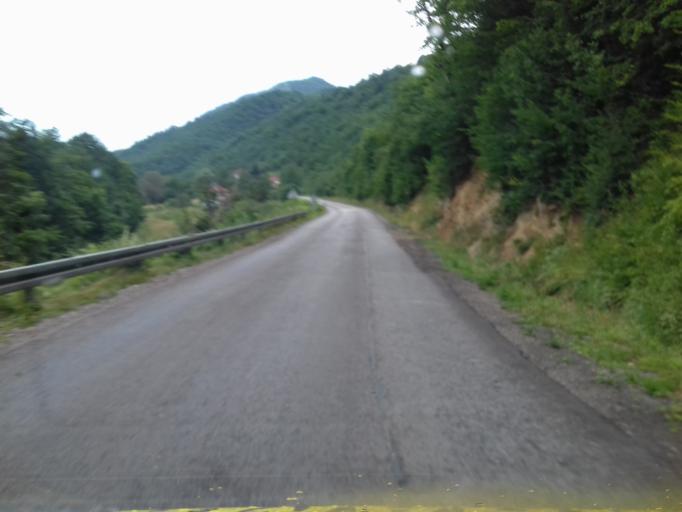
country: BA
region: Federation of Bosnia and Herzegovina
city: Visoko
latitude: 43.9564
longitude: 18.1642
